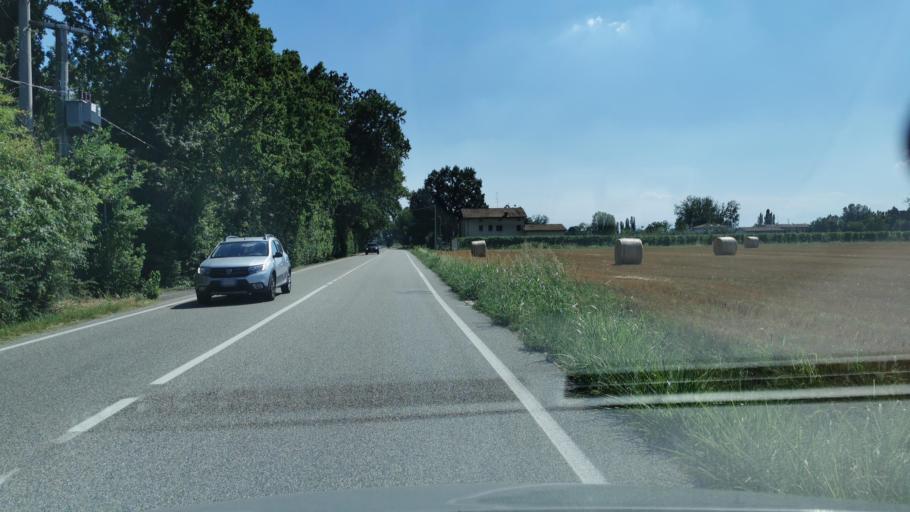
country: IT
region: Emilia-Romagna
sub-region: Provincia di Modena
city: Sam Marino
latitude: 44.7909
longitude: 10.9103
